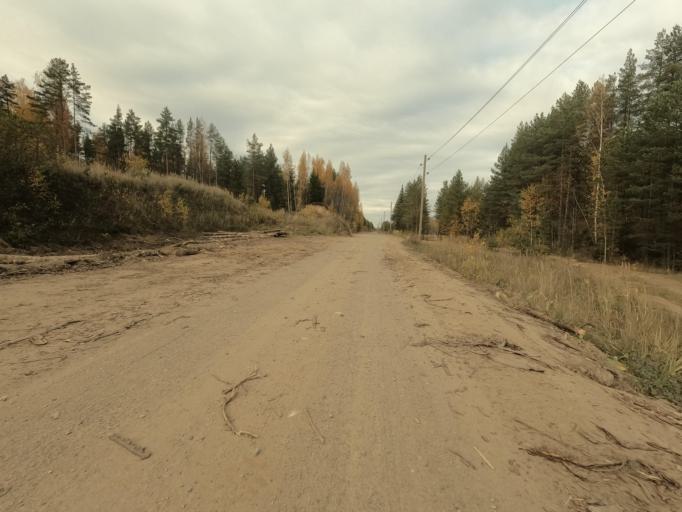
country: RU
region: Leningrad
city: Priladozhskiy
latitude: 59.6919
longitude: 31.3610
